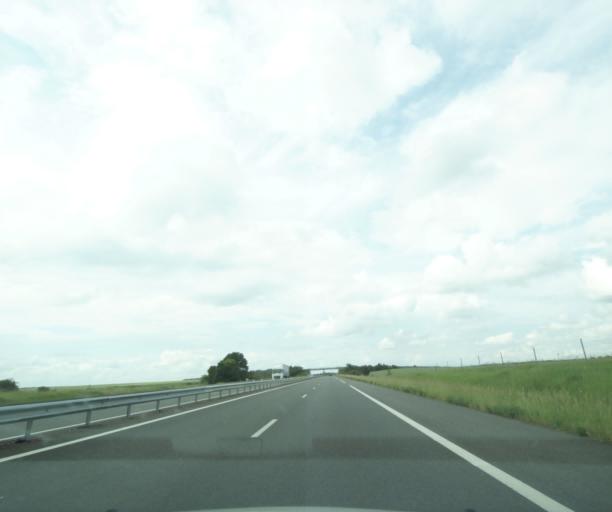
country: FR
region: Centre
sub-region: Departement du Cher
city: Chateauneuf-sur-Cher
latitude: 46.8224
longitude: 2.4129
